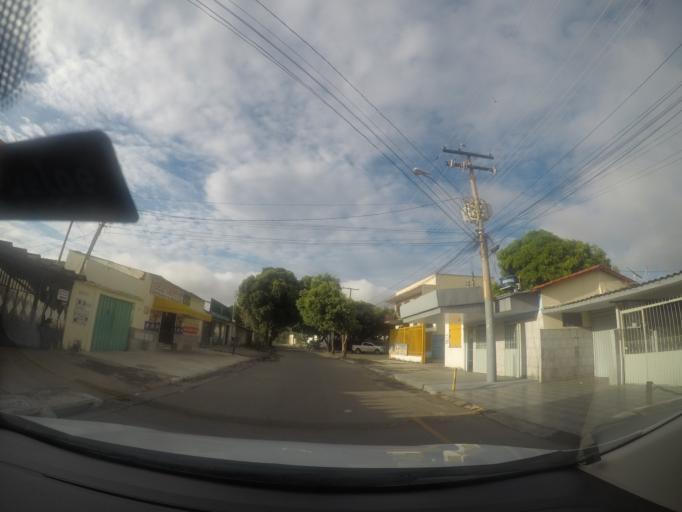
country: BR
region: Goias
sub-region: Goiania
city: Goiania
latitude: -16.6825
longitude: -49.3115
